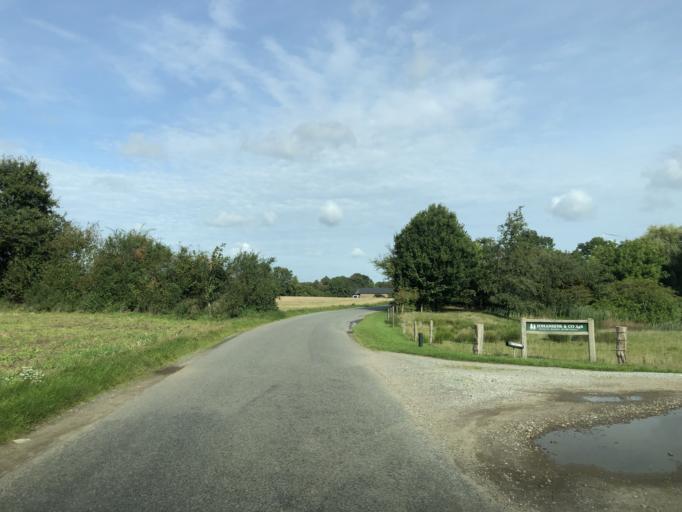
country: DK
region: South Denmark
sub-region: Vejle Kommune
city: Borkop
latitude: 55.6130
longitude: 9.6720
